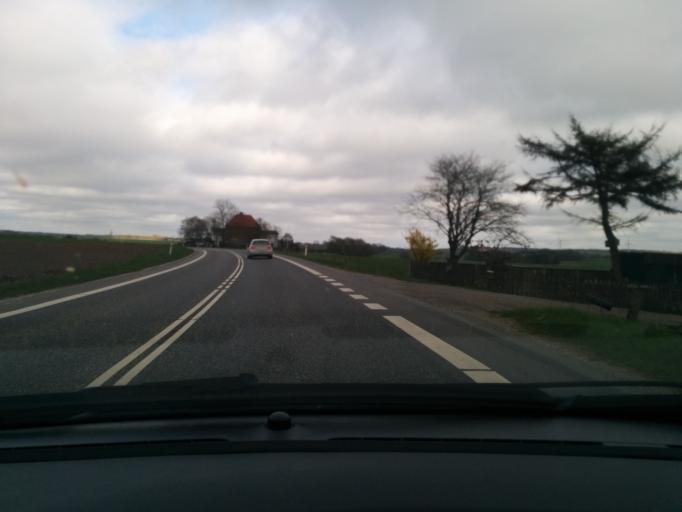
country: DK
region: Central Jutland
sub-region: Favrskov Kommune
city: Hammel
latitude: 56.2097
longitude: 9.8111
